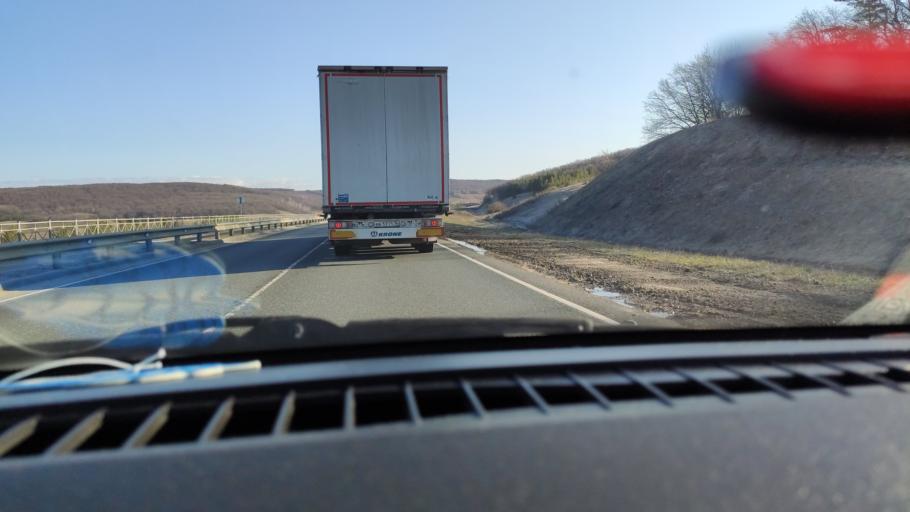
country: RU
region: Saratov
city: Alekseyevka
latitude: 52.3893
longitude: 47.9760
